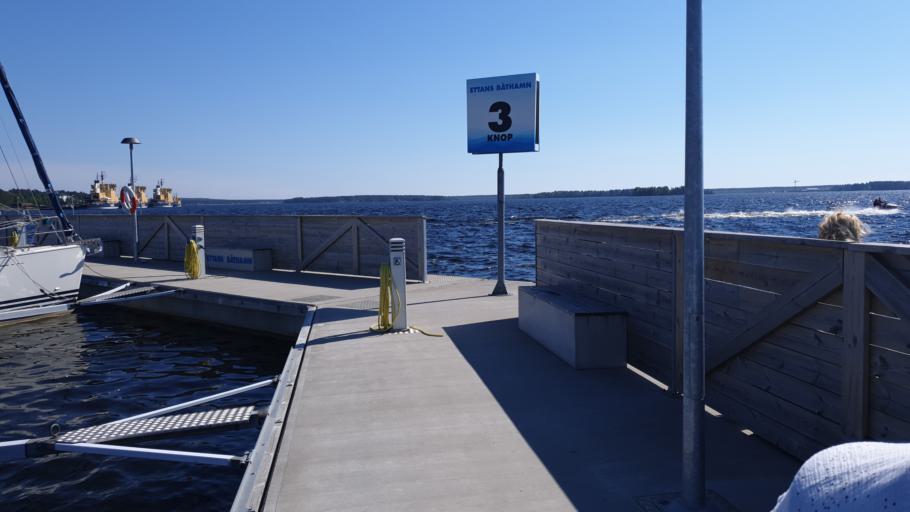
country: SE
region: Norrbotten
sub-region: Lulea Kommun
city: Lulea
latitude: 65.5788
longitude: 22.1609
